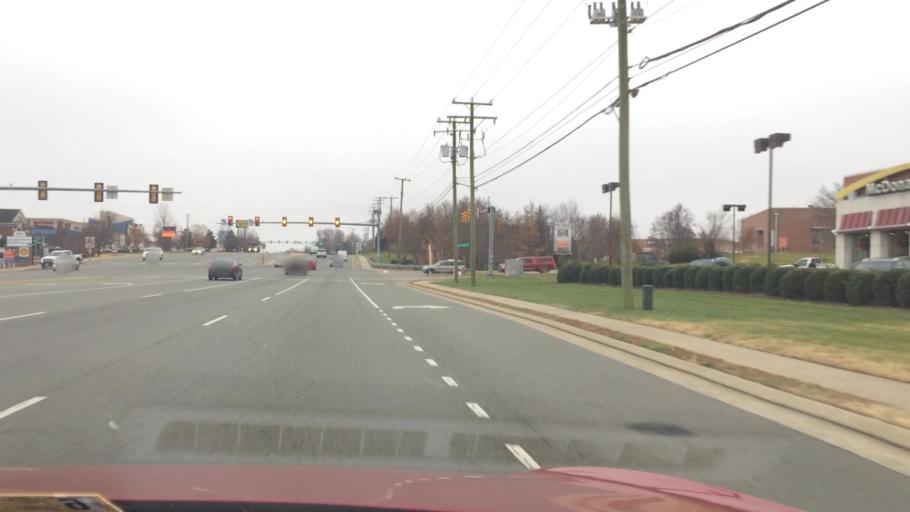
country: US
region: Virginia
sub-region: Henrico County
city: Glen Allen
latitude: 37.6723
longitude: -77.4610
